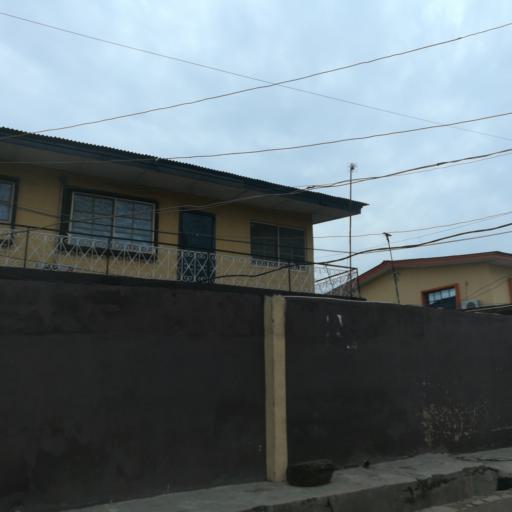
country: NG
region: Lagos
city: Ikeja
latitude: 6.5994
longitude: 3.3458
